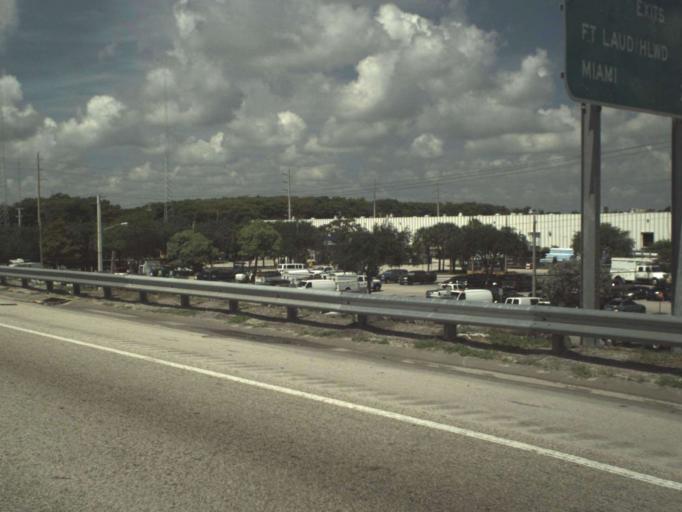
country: US
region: Florida
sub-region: Broward County
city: Twin Lakes
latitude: 26.1757
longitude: -80.1558
